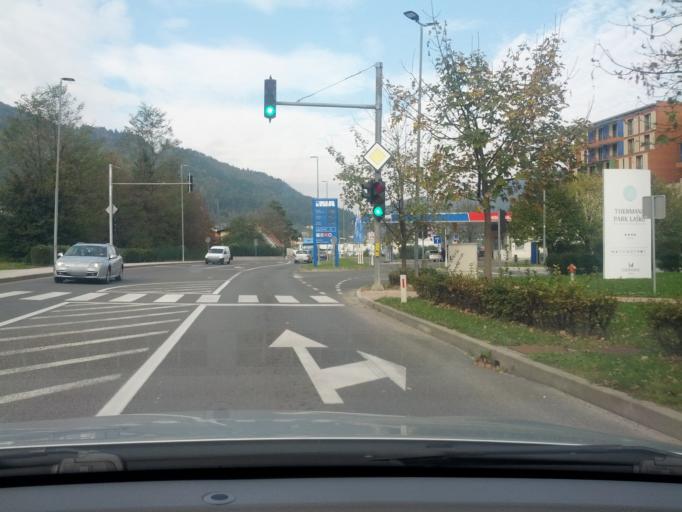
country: SI
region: Lasko
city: Lasko
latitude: 46.1615
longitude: 15.2313
